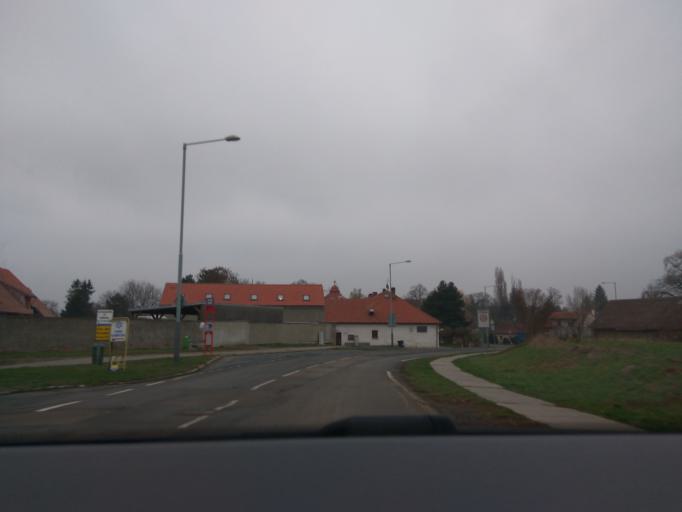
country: CZ
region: Central Bohemia
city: Hovorcovice
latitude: 50.1641
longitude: 14.5244
